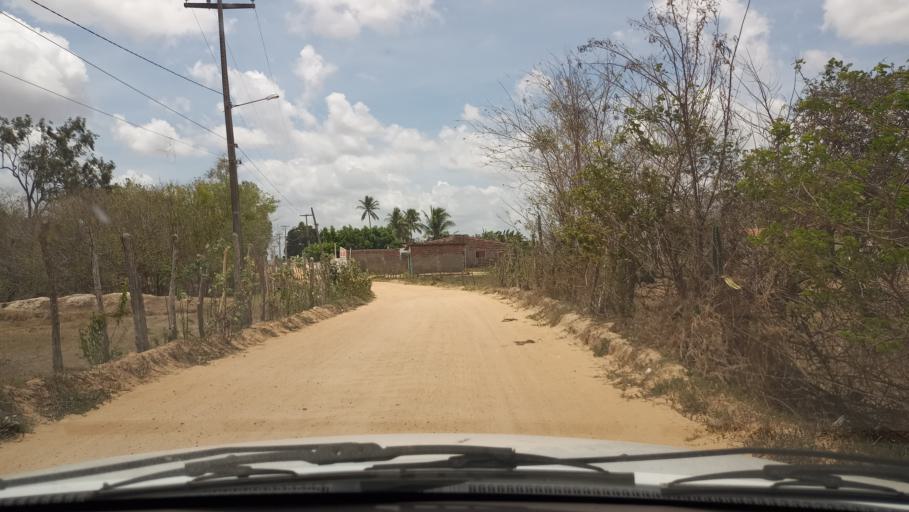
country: BR
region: Rio Grande do Norte
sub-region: Brejinho
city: Brejinho
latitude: -6.2934
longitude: -35.3442
